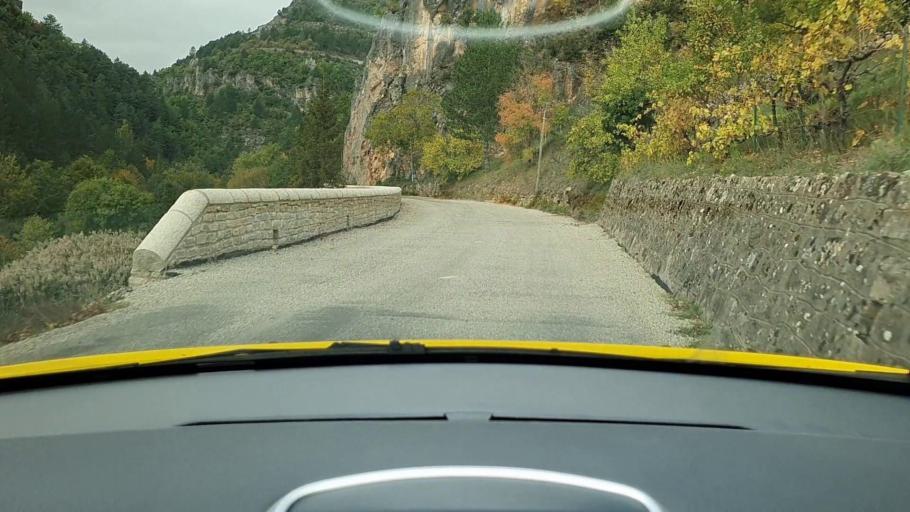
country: FR
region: Languedoc-Roussillon
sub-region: Departement de la Lozere
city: Meyrueis
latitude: 44.0788
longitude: 3.3840
